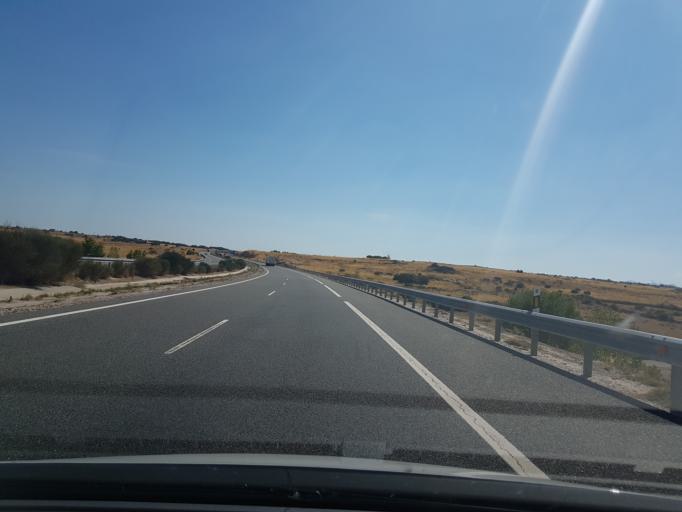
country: ES
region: Castille and Leon
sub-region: Provincia de Avila
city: Cardenosa
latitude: 40.7122
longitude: -4.7471
